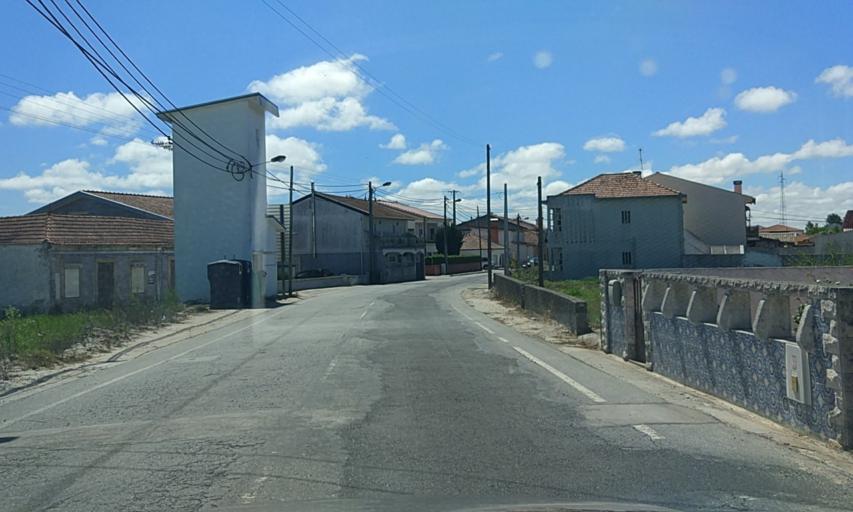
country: PT
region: Aveiro
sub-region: Ilhavo
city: Ilhavo
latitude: 40.6136
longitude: -8.6841
